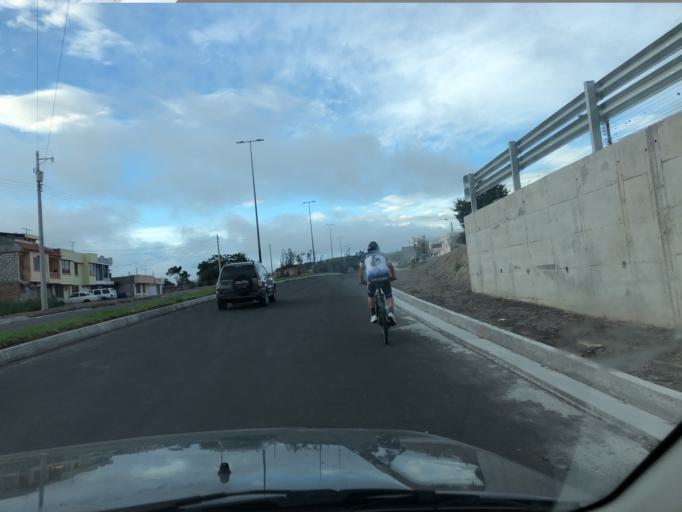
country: EC
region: Imbabura
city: Ibarra
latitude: 0.3516
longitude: -78.1408
